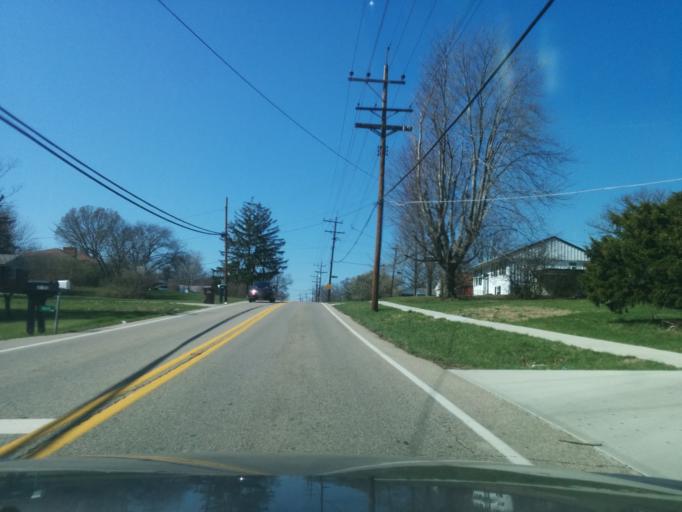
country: US
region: Ohio
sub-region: Hamilton County
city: Northgate
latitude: 39.2356
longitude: -84.6053
